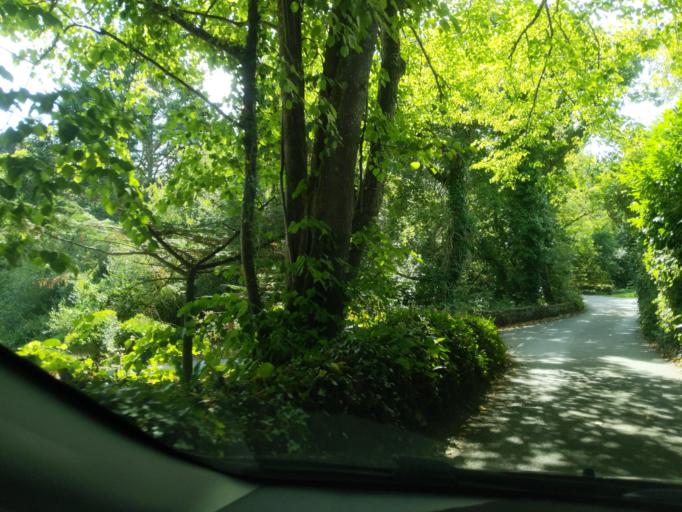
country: GB
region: England
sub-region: Cornwall
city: Torpoint
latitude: 50.3622
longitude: -4.2397
